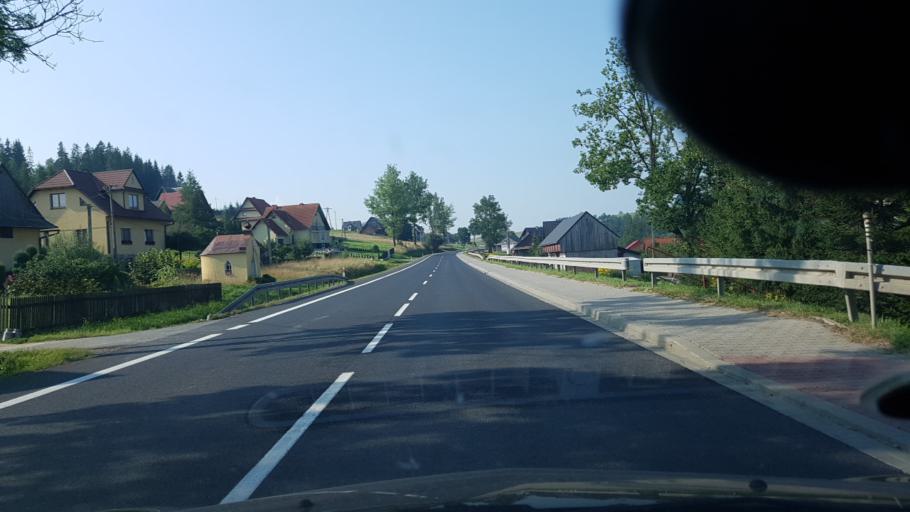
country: PL
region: Lesser Poland Voivodeship
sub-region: Powiat nowotarski
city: Podwilk
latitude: 49.5320
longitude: 19.7146
